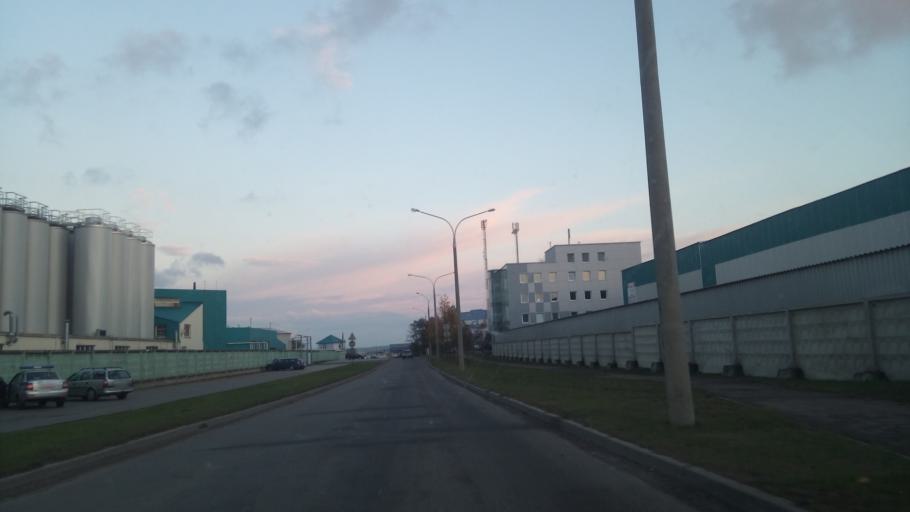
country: BY
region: Minsk
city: Vyaliki Trastsyanets
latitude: 53.8658
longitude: 27.6959
